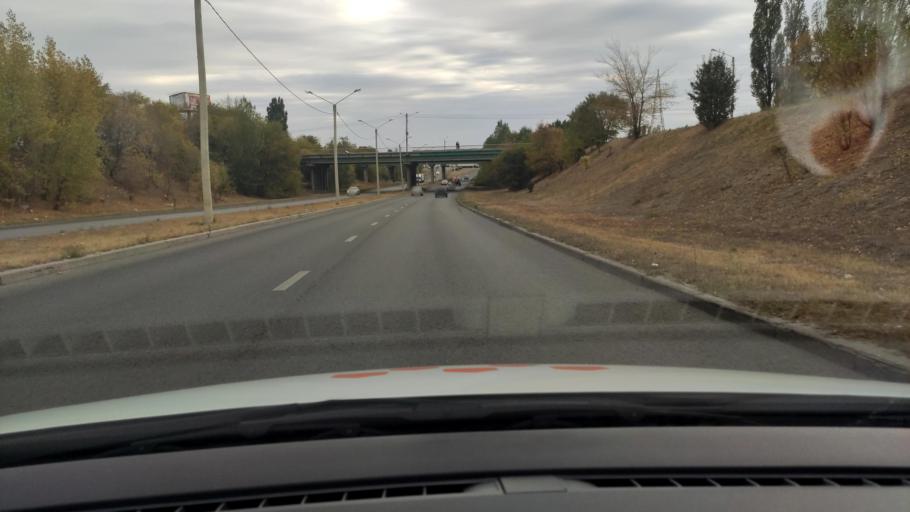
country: RU
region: Voronezj
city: Voronezh
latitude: 51.6472
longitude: 39.1366
